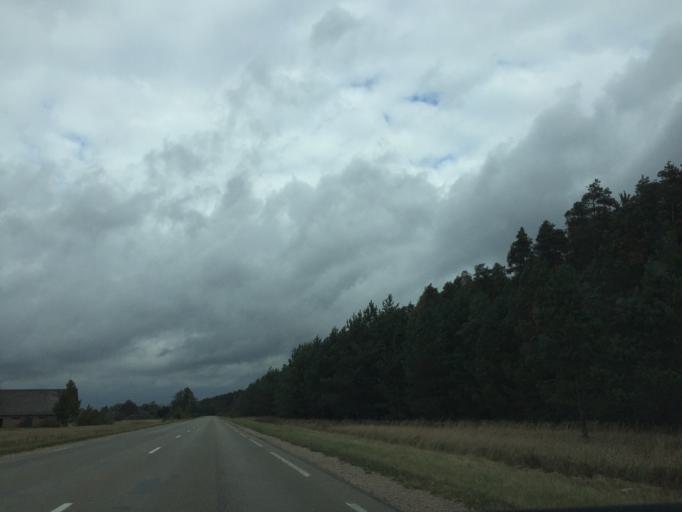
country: LV
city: Tireli
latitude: 56.8139
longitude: 23.6196
